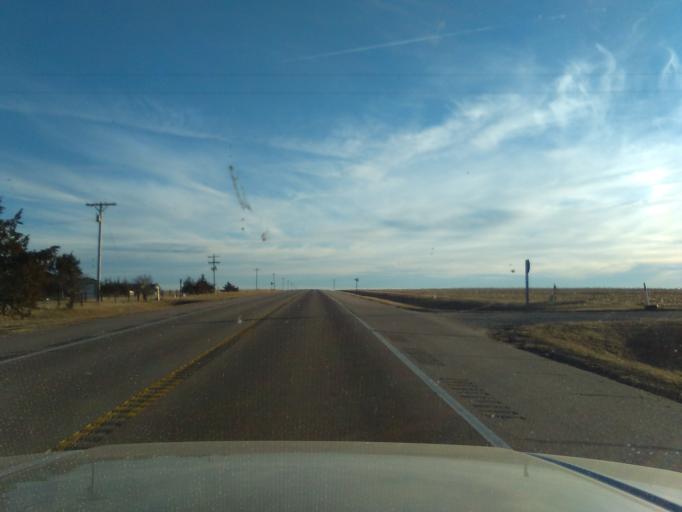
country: US
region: Kansas
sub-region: Logan County
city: Oakley
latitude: 39.1770
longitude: -100.8704
